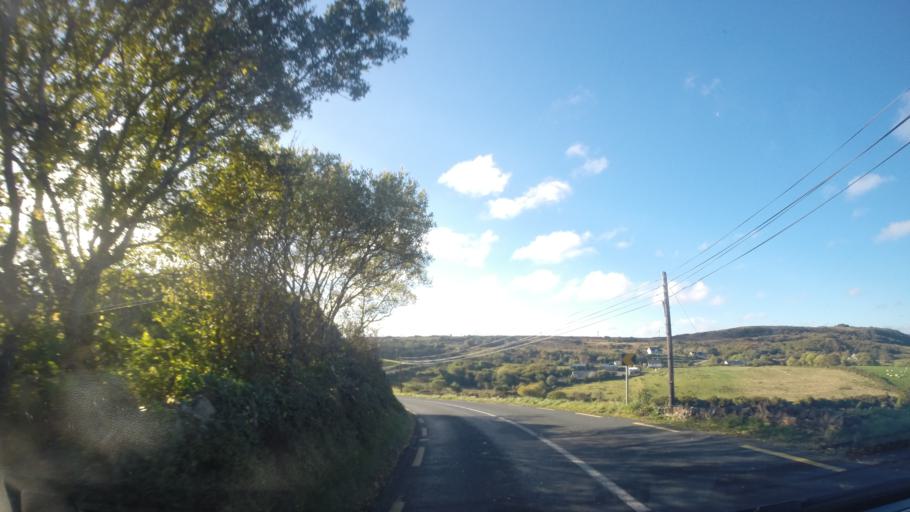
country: IE
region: Ulster
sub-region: County Donegal
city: Dungloe
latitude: 54.8337
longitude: -8.3662
